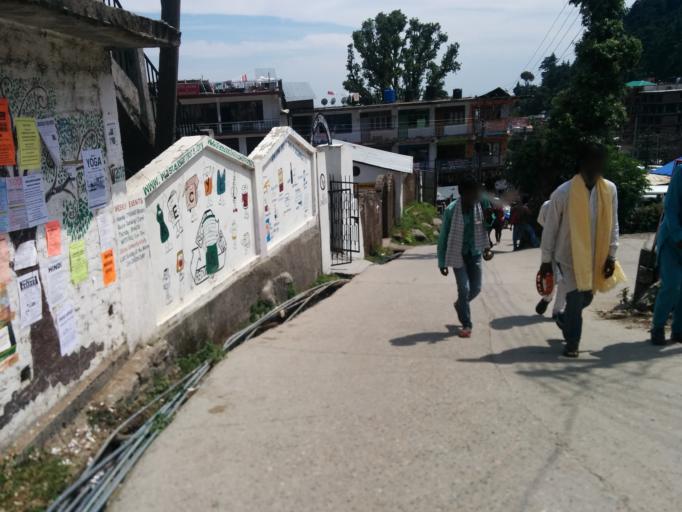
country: IN
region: Himachal Pradesh
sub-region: Kangra
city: Dharmsala
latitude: 32.2442
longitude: 76.3332
